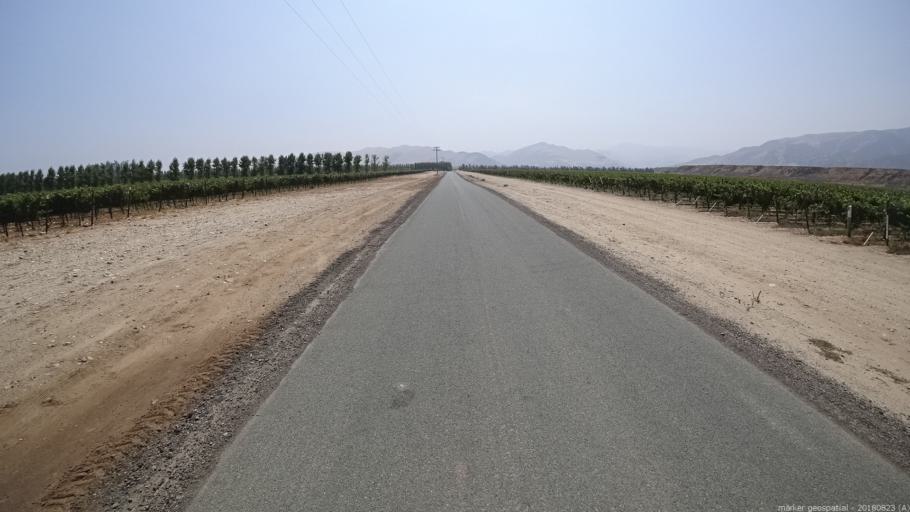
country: US
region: California
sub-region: Monterey County
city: Greenfield
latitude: 36.3272
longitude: -121.2960
